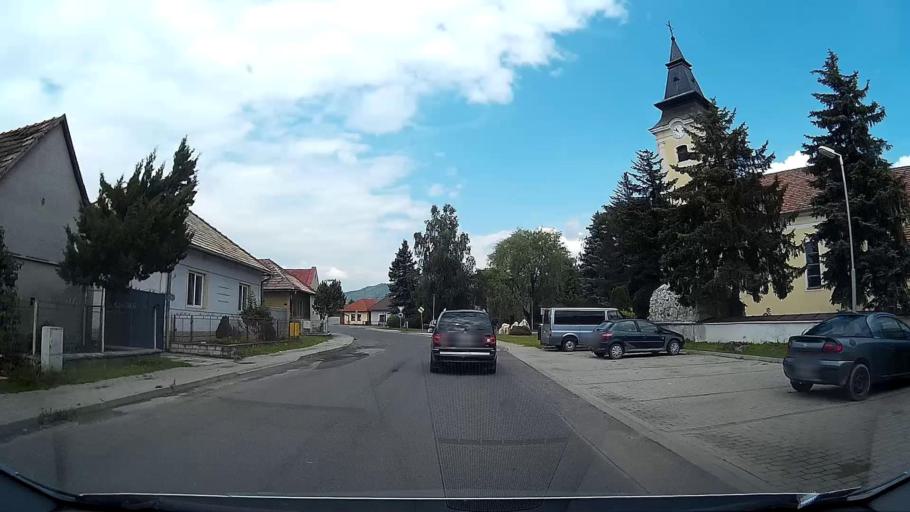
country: SK
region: Presovsky
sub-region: Okres Poprad
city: Poprad
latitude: 48.9942
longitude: 20.3588
